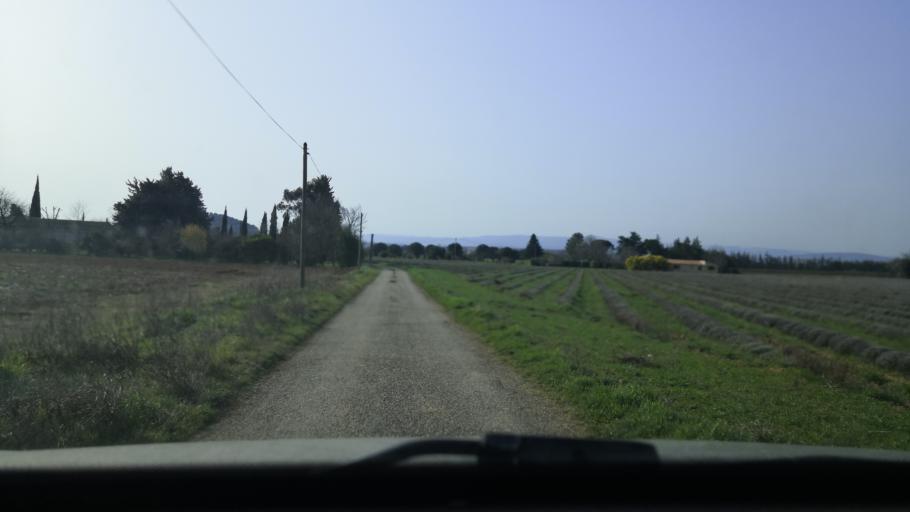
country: FR
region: Rhone-Alpes
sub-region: Departement de la Drome
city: La Begude-de-Mazenc
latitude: 44.5573
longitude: 4.8873
